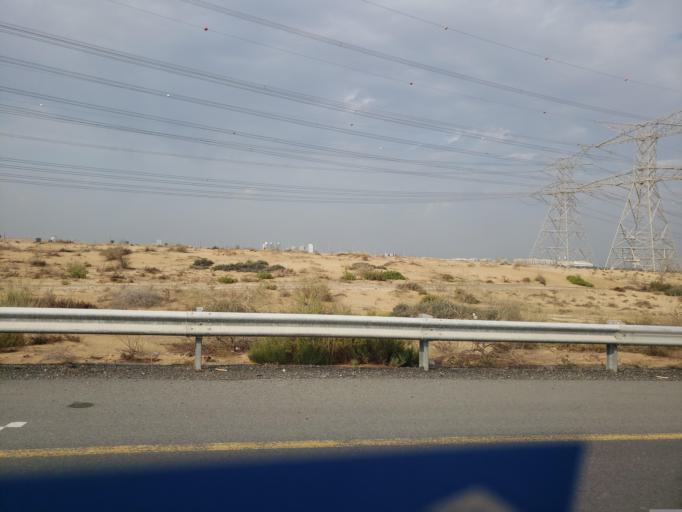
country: AE
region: Dubai
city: Dubai
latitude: 24.9808
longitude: 55.2401
